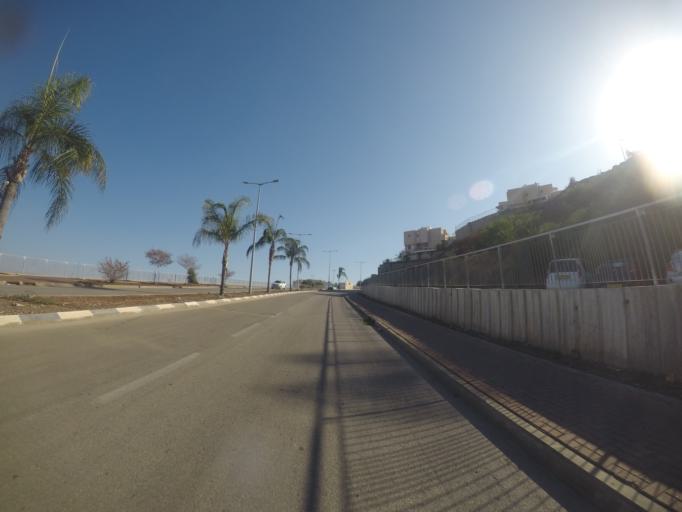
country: IL
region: Northern District
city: Tiberias
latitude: 32.7845
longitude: 35.5304
